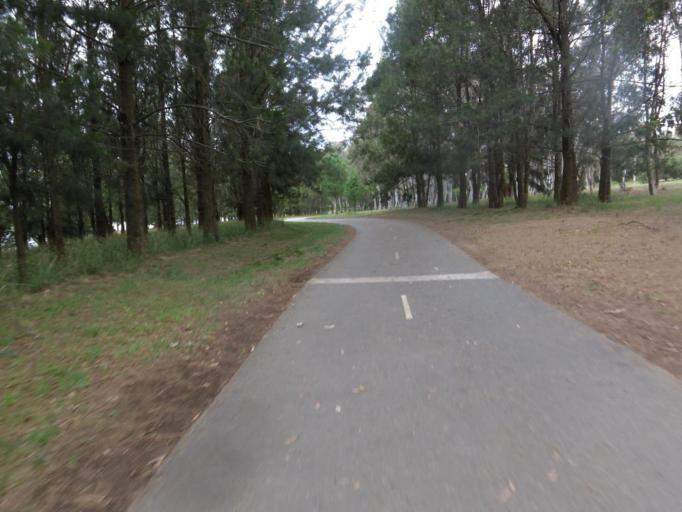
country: AU
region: Australian Capital Territory
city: Kaleen
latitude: -35.1797
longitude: 149.1284
